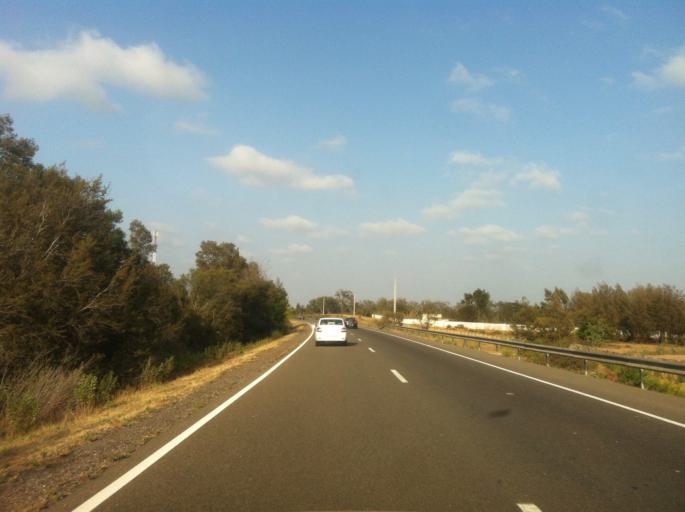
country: MA
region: Gharb-Chrarda-Beni Hssen
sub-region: Kenitra Province
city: Kenitra
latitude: 34.2298
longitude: -6.5760
